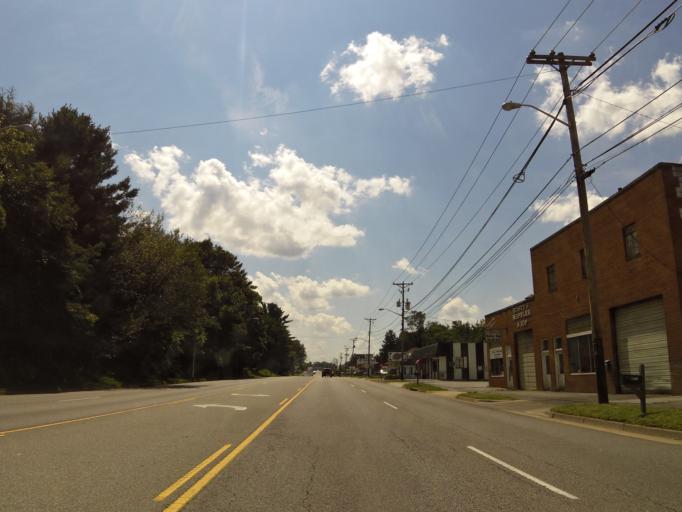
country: US
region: Virginia
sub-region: Washington County
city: Abingdon
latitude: 36.7042
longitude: -81.9991
